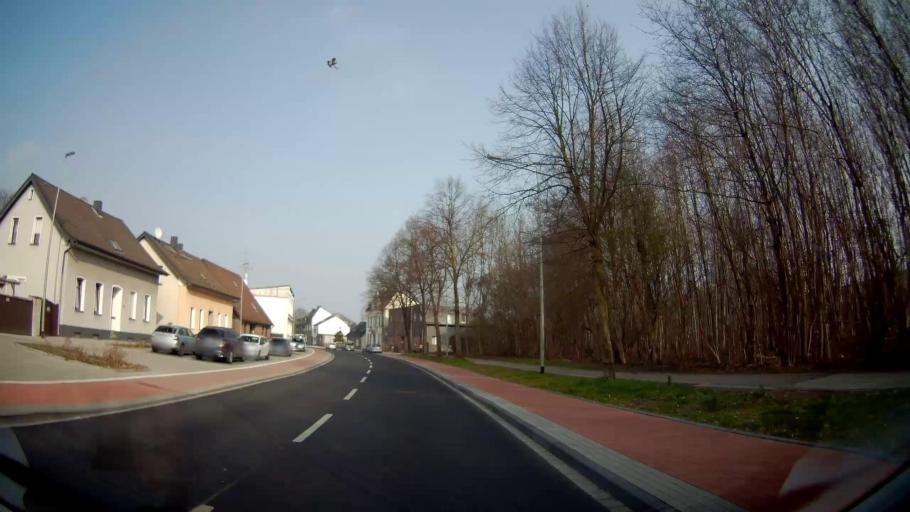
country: DE
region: North Rhine-Westphalia
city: Meiderich
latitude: 51.4599
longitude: 6.8067
